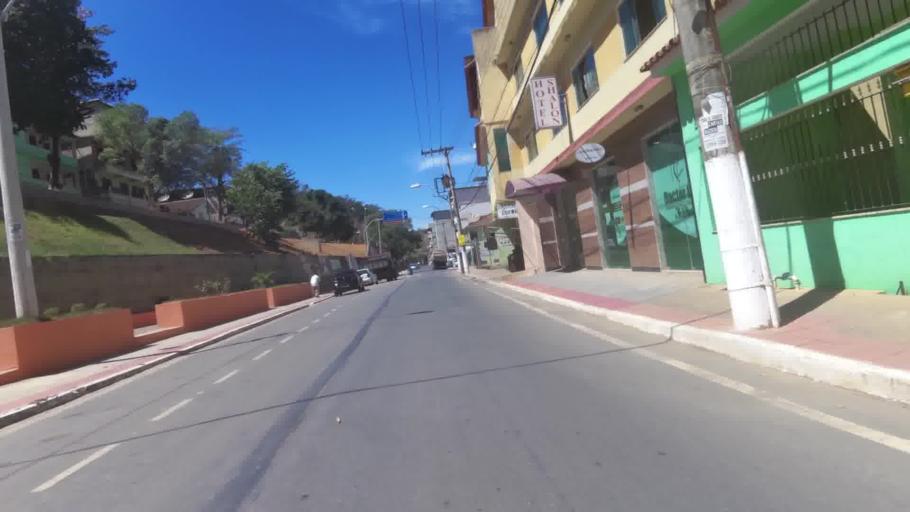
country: BR
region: Espirito Santo
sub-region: Cachoeiro De Itapemirim
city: Cachoeiro de Itapemirim
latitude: -20.9146
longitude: -41.1932
